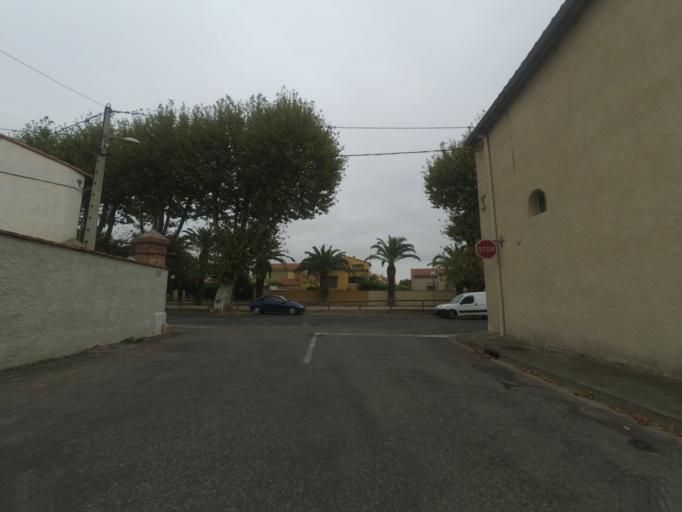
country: FR
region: Languedoc-Roussillon
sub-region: Departement des Pyrenees-Orientales
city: Saint-Esteve
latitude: 42.7056
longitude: 2.8466
